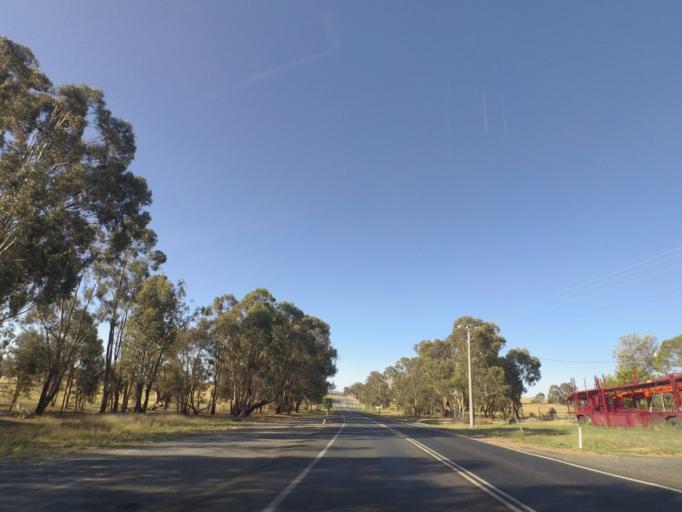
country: AU
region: New South Wales
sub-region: Wagga Wagga
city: Forest Hill
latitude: -35.2705
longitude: 147.7445
